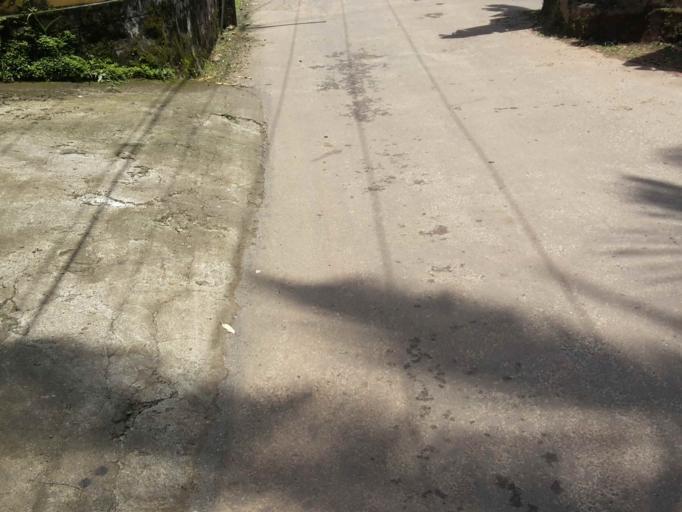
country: IN
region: Kerala
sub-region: Kozhikode
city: Kozhikode
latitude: 11.2836
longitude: 75.7923
